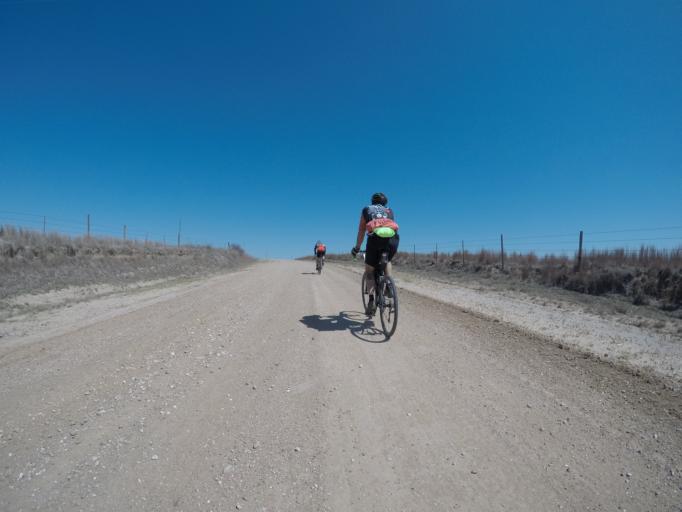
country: US
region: Kansas
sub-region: Pratt County
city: Pratt
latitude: 37.4062
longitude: -98.8405
